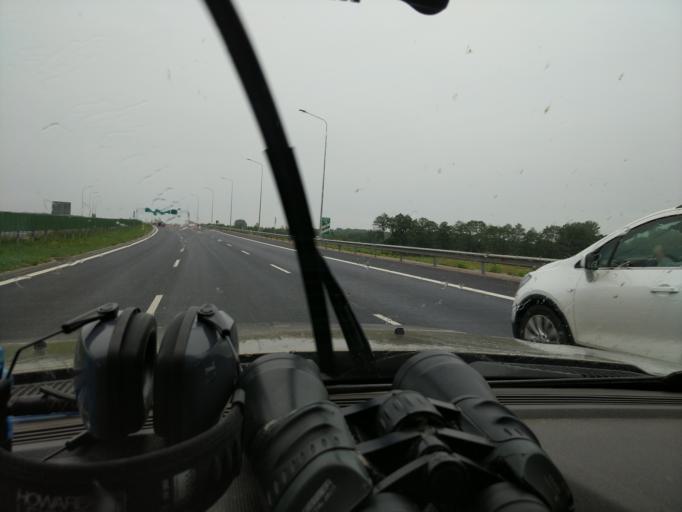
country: PL
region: Masovian Voivodeship
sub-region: Powiat wolominski
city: Kobylka
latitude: 52.3657
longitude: 21.1894
